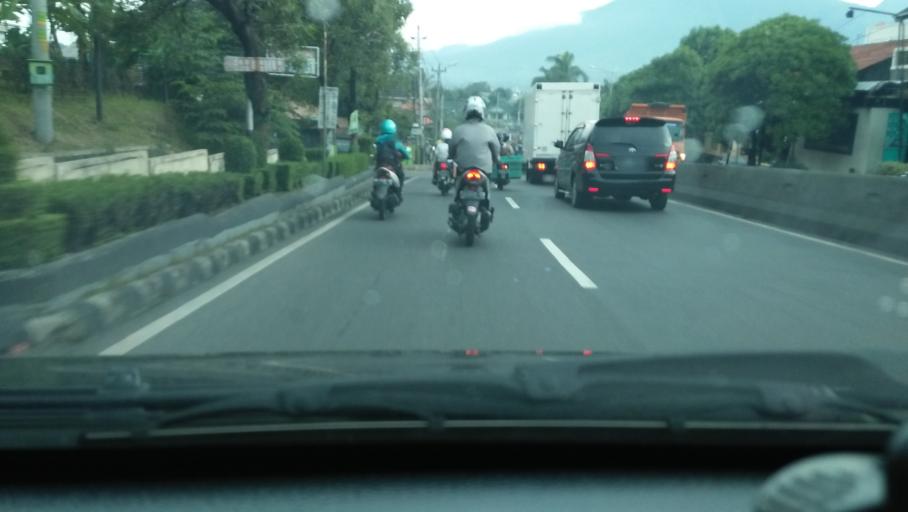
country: ID
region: Central Java
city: Ungaran
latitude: -7.1172
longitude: 110.4129
